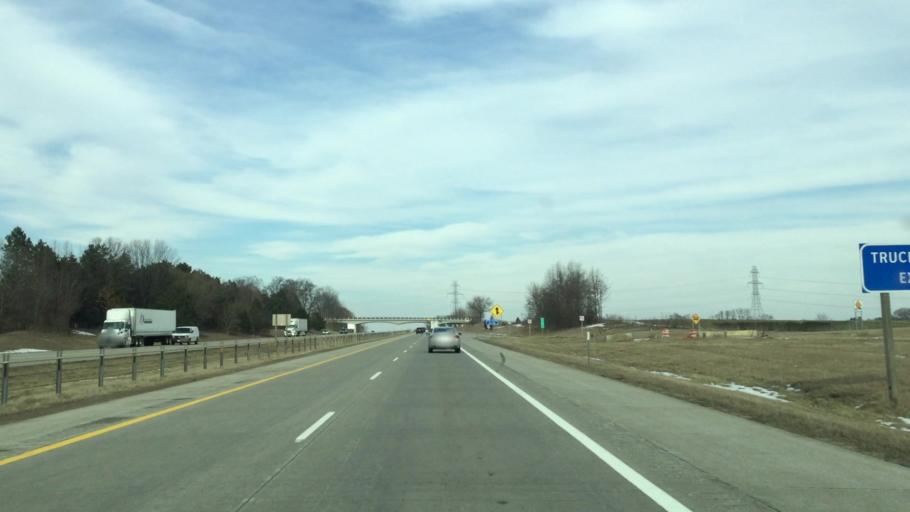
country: US
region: Michigan
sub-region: Berrien County
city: Coloma
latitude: 42.1542
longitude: -86.3397
